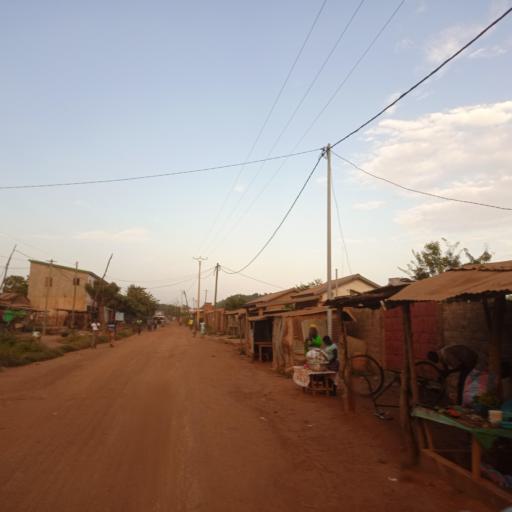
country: TG
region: Savanes
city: Dapaong
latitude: 10.8619
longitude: 0.1856
